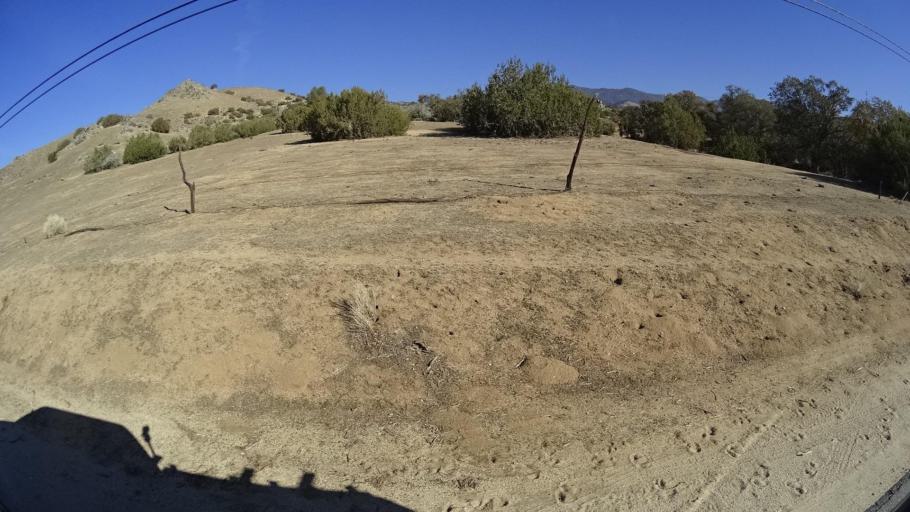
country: US
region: California
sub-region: Kern County
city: Bodfish
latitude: 35.3686
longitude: -118.3923
